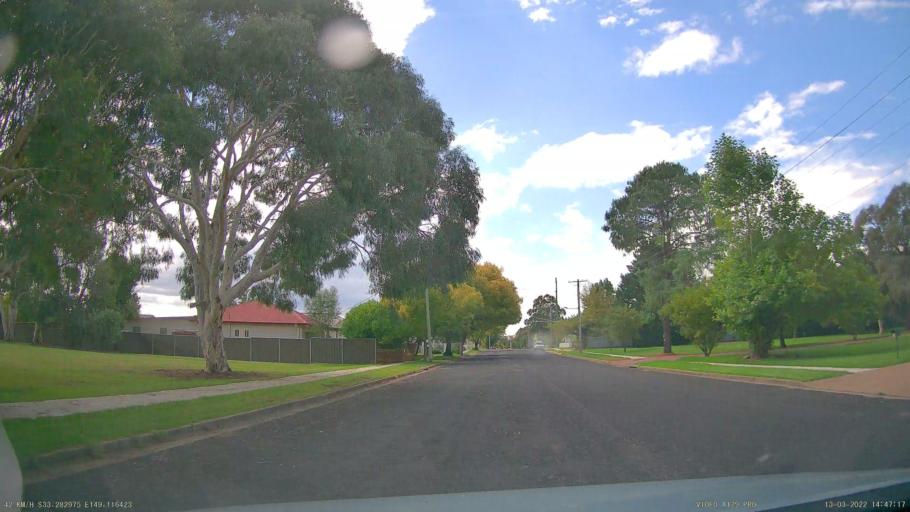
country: AU
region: New South Wales
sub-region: Orange Municipality
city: Orange
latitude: -33.2829
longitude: 149.1164
